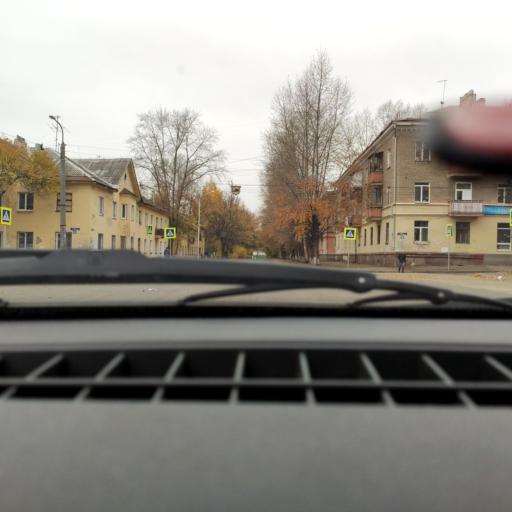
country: RU
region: Bashkortostan
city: Ufa
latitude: 54.8191
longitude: 56.1014
